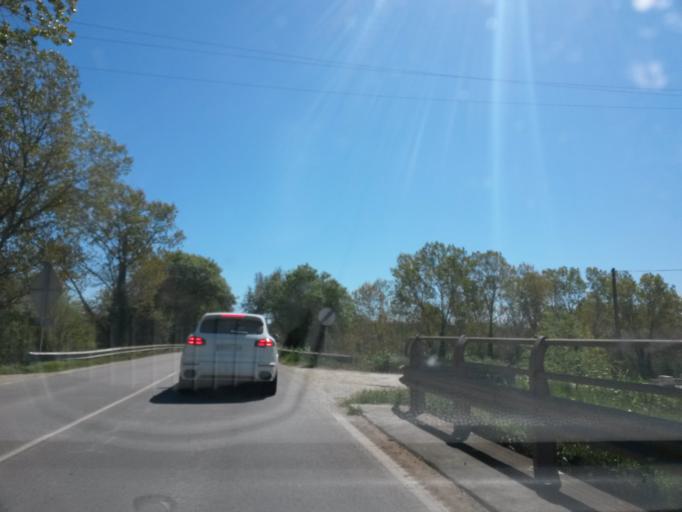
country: ES
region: Catalonia
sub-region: Provincia de Girona
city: Riudellots de la Selva
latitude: 41.8983
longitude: 2.8165
